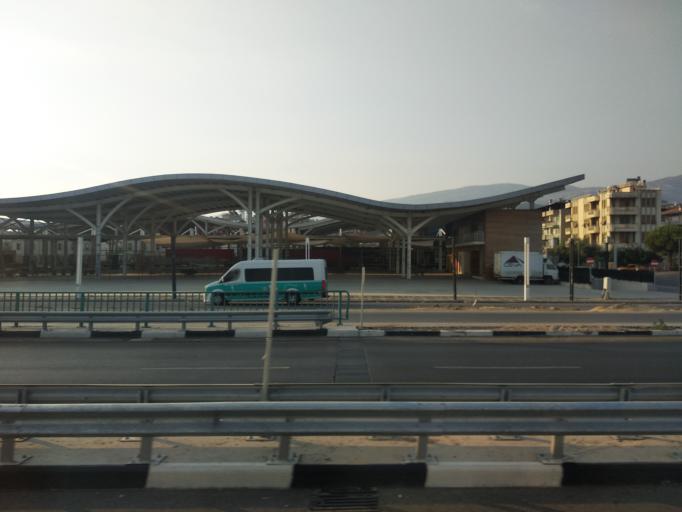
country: TR
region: Manisa
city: Salihli
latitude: 38.4877
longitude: 28.1325
